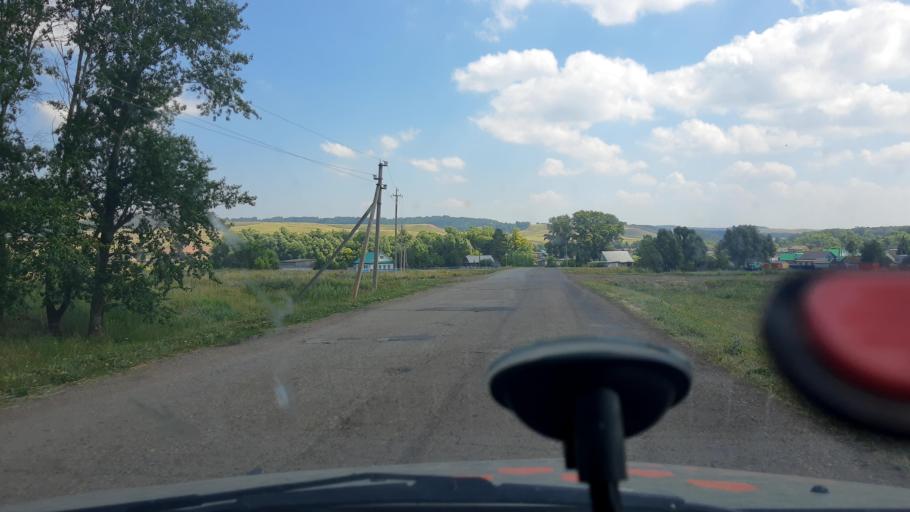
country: RU
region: Bashkortostan
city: Chekmagush
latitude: 54.8832
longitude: 54.6017
